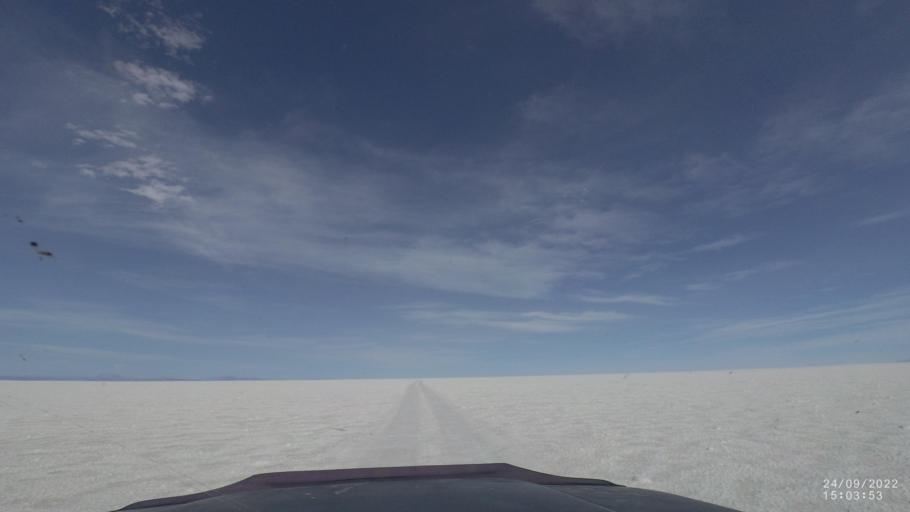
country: BO
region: Potosi
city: Colchani
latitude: -19.8971
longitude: -67.5275
